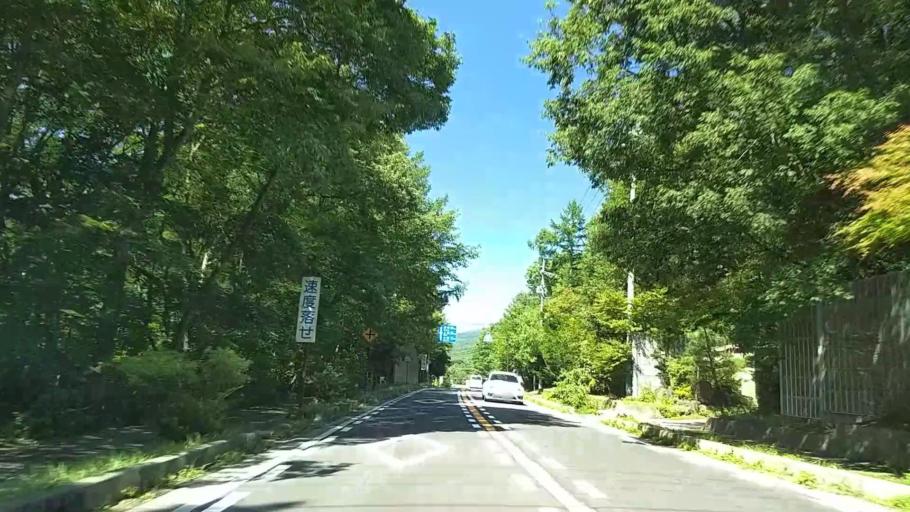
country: JP
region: Nagano
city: Komoro
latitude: 36.3388
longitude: 138.5339
